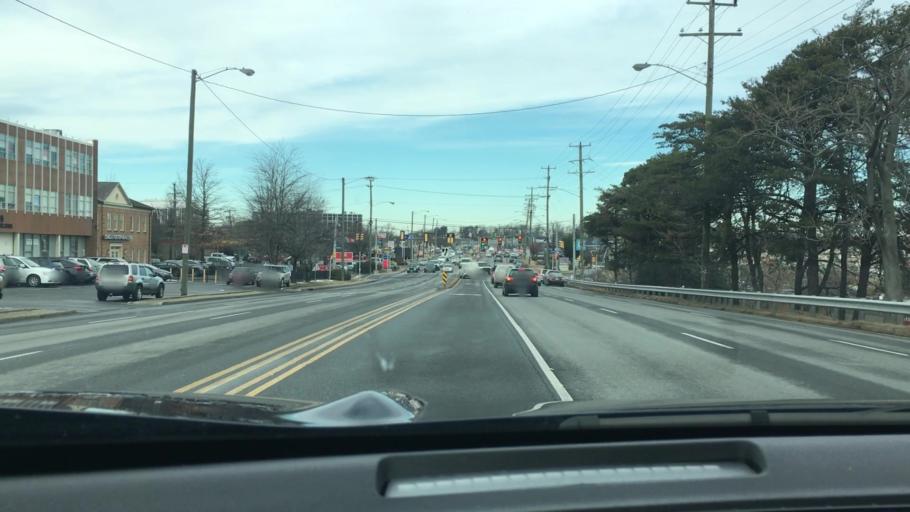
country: US
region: Virginia
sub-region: Fairfax County
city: Seven Corners
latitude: 38.8693
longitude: -77.1536
